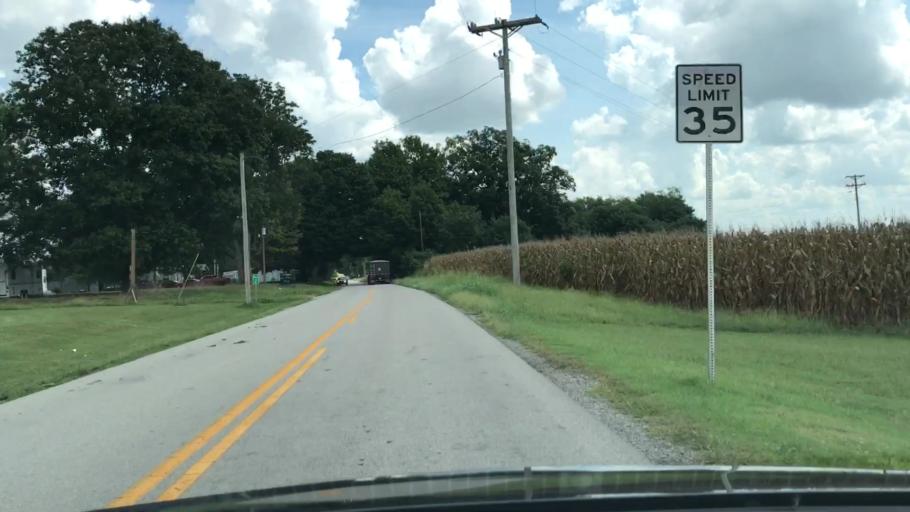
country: US
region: Kentucky
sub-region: Todd County
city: Guthrie
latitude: 36.6523
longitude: -87.0140
